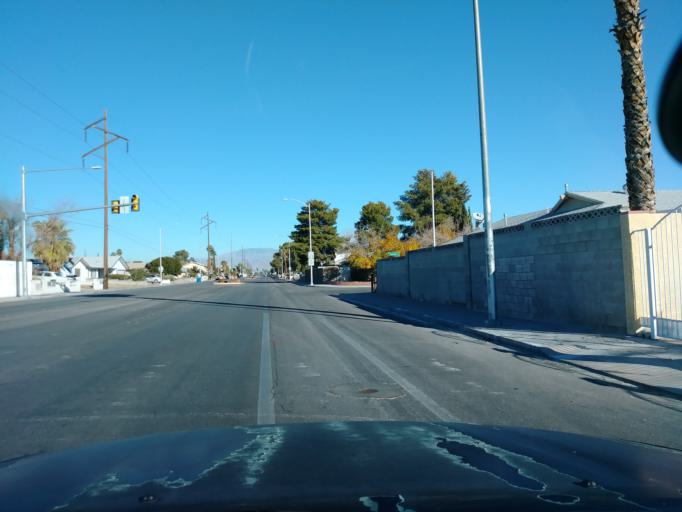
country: US
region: Nevada
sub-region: Clark County
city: Spring Valley
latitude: 36.1698
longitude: -115.2508
